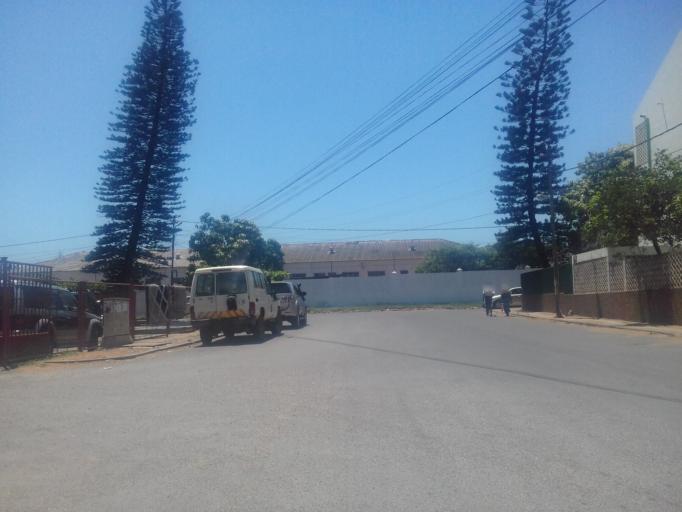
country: MZ
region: Maputo City
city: Maputo
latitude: -25.9544
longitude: 32.5901
